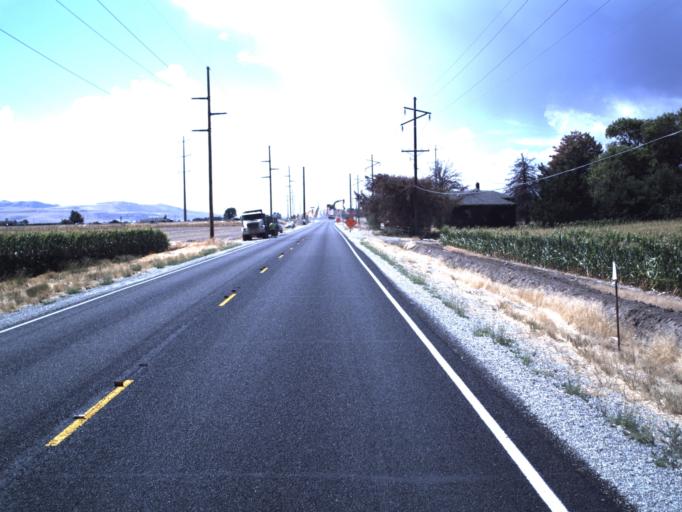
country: US
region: Utah
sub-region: Box Elder County
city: Honeyville
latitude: 41.6349
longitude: -112.0932
